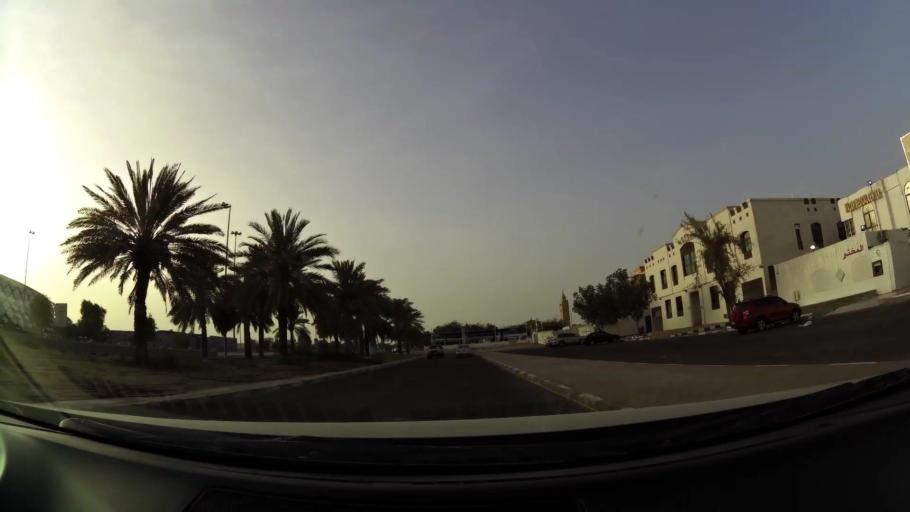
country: AE
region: Abu Dhabi
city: Al Ain
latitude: 24.2440
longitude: 55.7200
